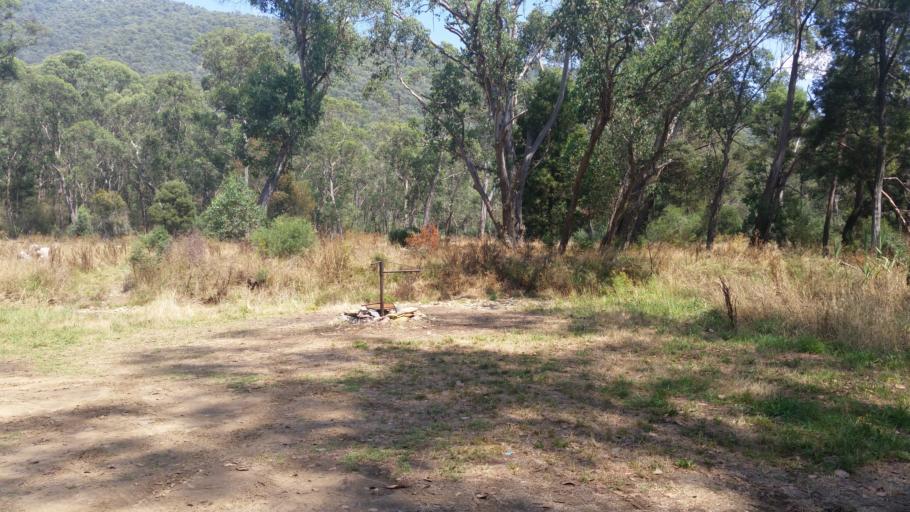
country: AU
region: Victoria
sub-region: Alpine
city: Mount Beauty
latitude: -36.7563
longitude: 147.0242
